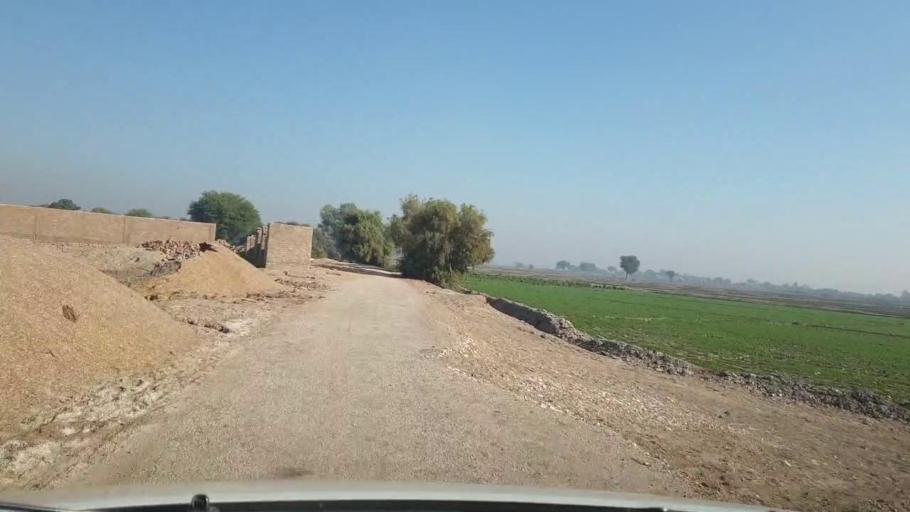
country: PK
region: Sindh
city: Dadu
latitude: 26.6720
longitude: 67.8388
